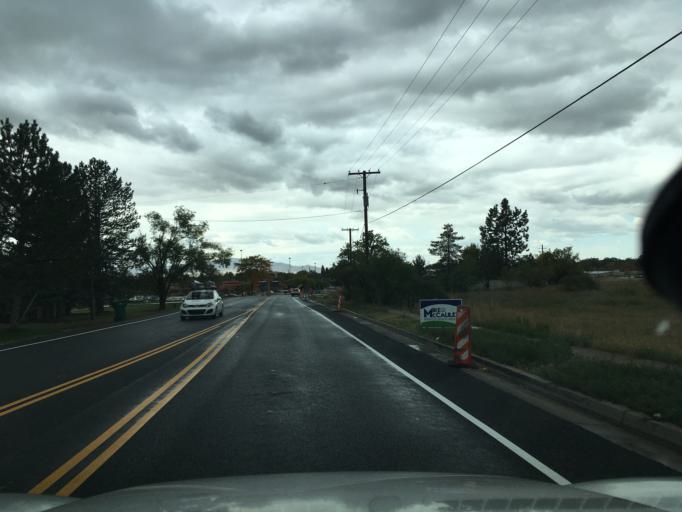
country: US
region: Utah
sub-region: Davis County
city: Kaysville
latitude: 41.0622
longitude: -111.9421
